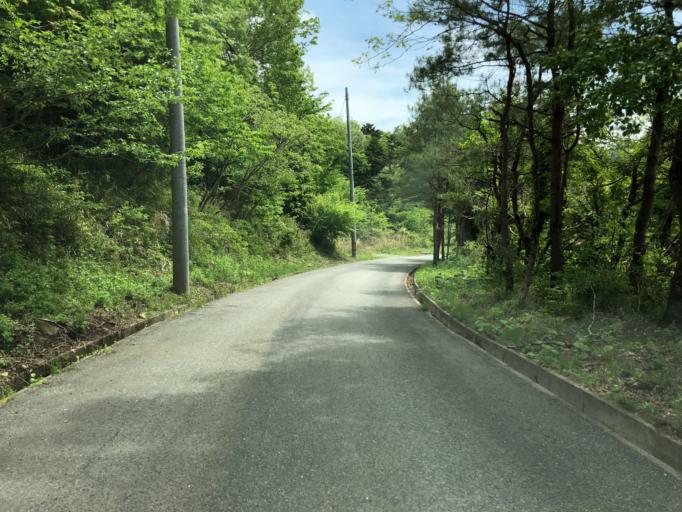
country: JP
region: Miyagi
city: Marumori
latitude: 37.7320
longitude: 140.8327
